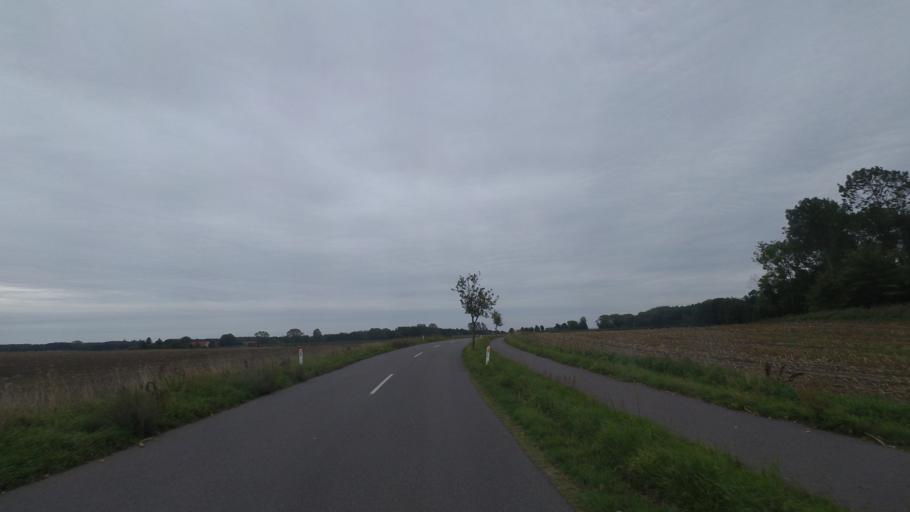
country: DK
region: Capital Region
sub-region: Bornholm Kommune
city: Akirkeby
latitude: 55.0072
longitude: 14.9975
